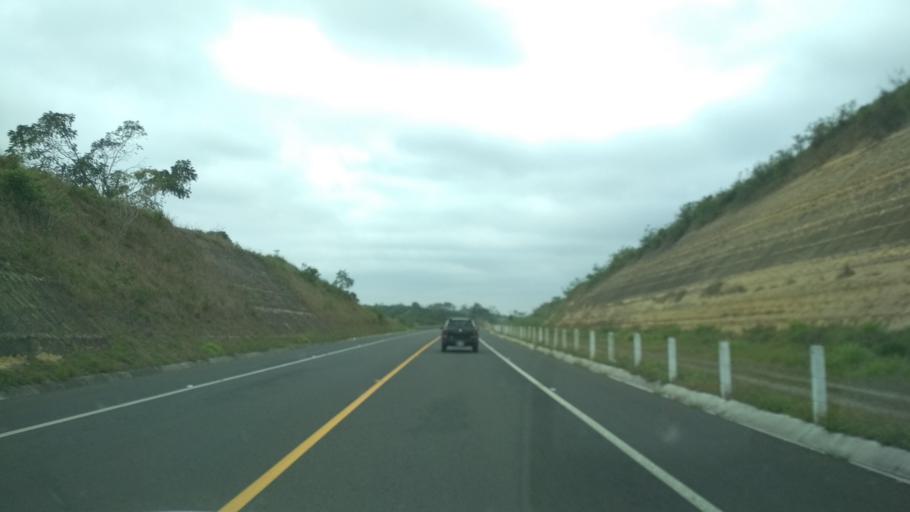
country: MX
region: Veracruz
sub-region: Papantla
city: Polutla
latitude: 20.4441
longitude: -97.2379
